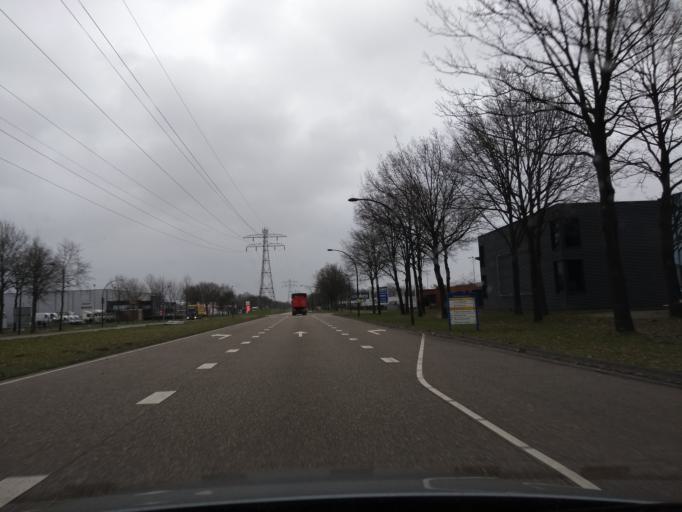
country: NL
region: Overijssel
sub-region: Gemeente Hengelo
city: Hengelo
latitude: 52.2420
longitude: 6.7678
